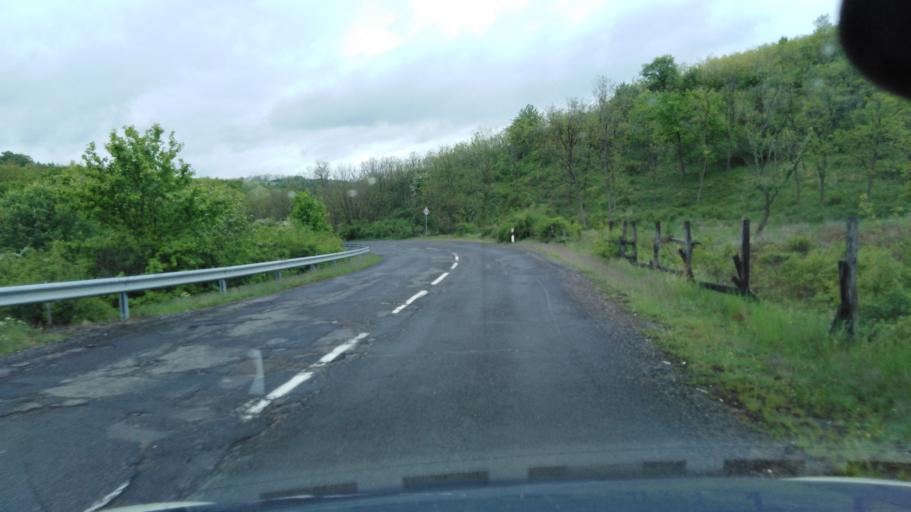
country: HU
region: Nograd
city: Rimoc
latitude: 48.0210
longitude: 19.5934
